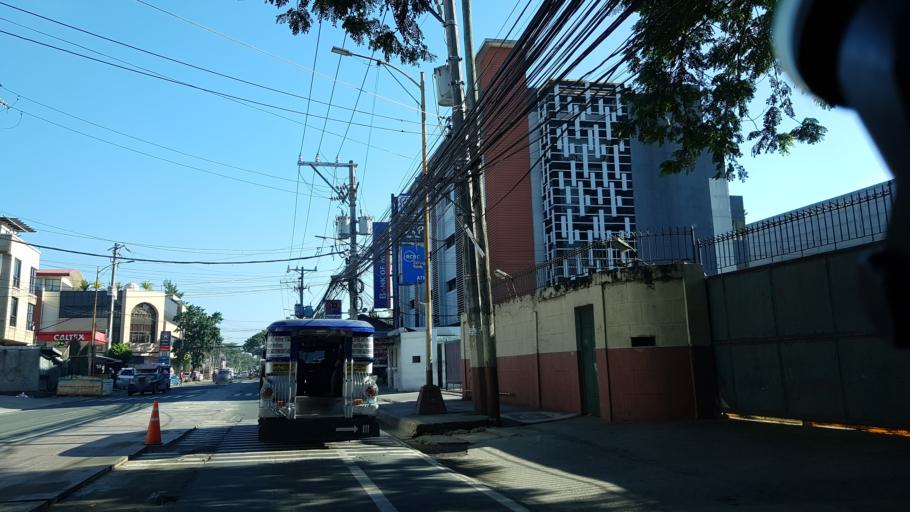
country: PH
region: Metro Manila
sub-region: Pasig
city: Pasig City
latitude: 14.5846
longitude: 121.0881
